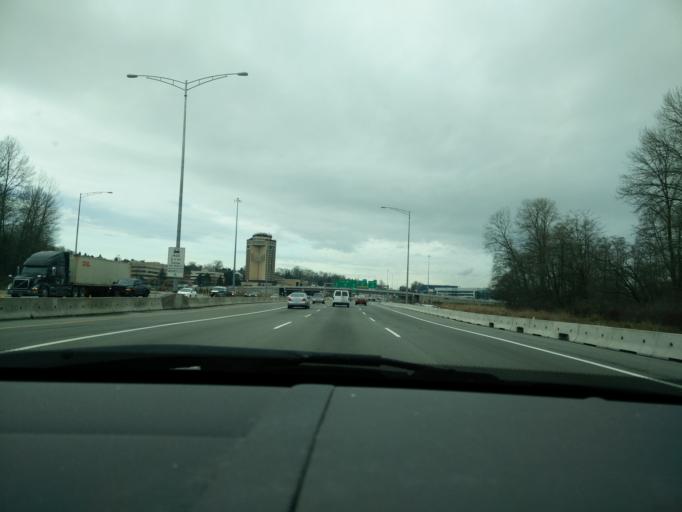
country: CA
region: British Columbia
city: Burnaby
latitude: 49.2579
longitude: -122.9980
